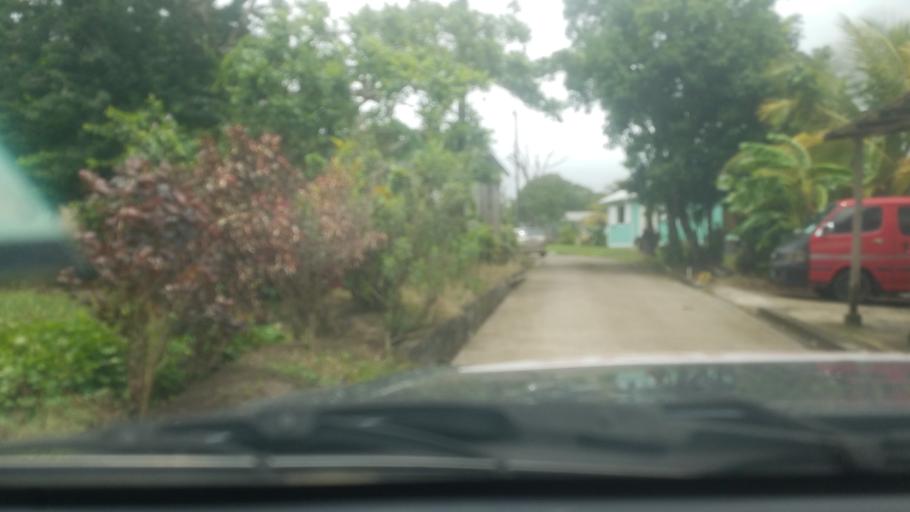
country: LC
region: Laborie Quarter
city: Laborie
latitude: 13.7788
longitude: -60.9989
